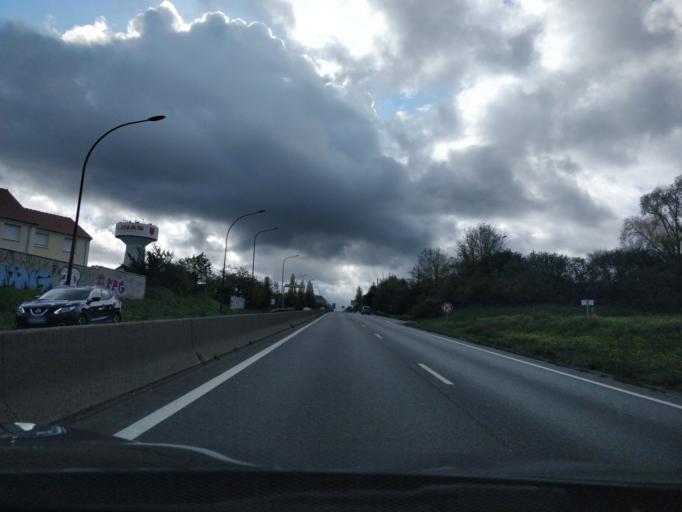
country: FR
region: Ile-de-France
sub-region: Departement de l'Essonne
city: Linas
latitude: 48.6287
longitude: 2.2627
